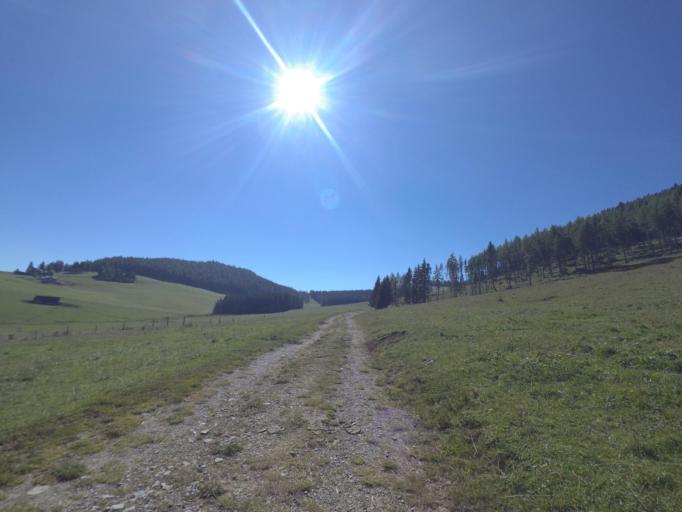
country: AT
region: Styria
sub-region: Politischer Bezirk Weiz
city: Passail
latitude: 47.3427
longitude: 15.4654
